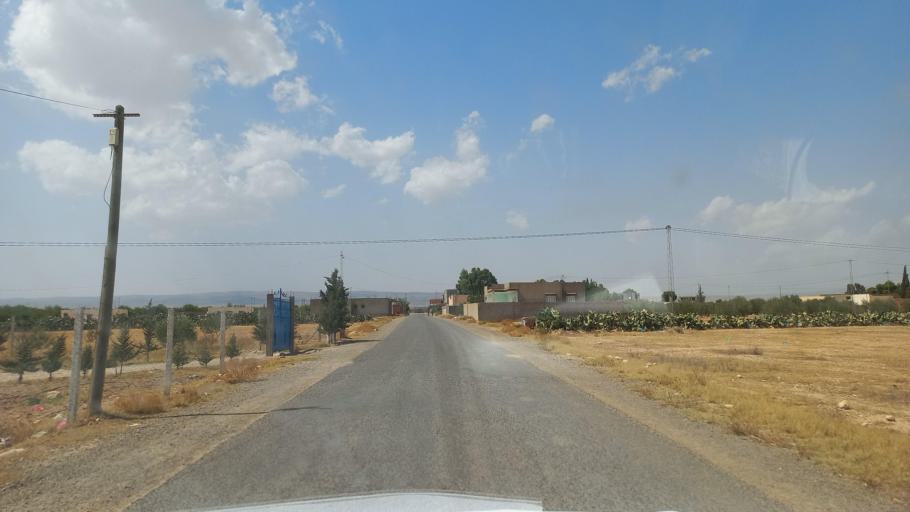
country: TN
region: Al Qasrayn
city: Kasserine
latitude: 35.2511
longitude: 9.0194
